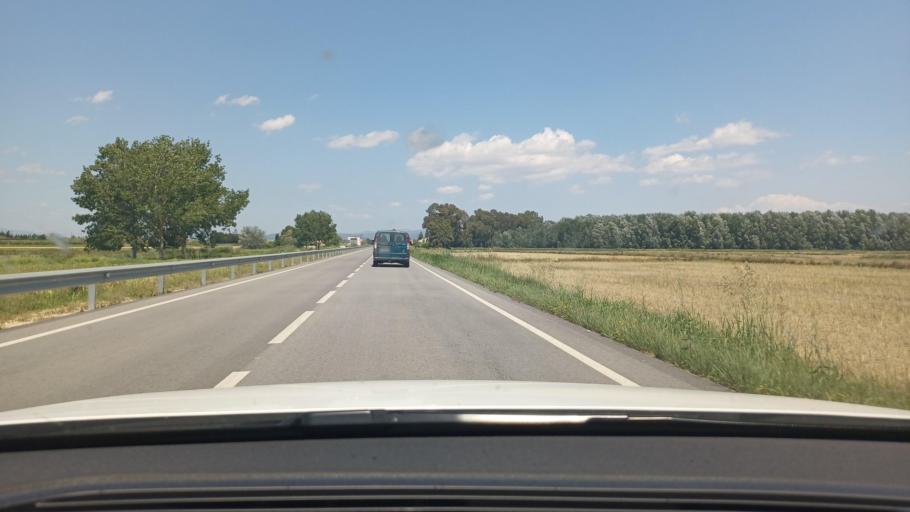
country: ES
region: Catalonia
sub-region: Provincia de Tarragona
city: Amposta
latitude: 40.6670
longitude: 0.5908
